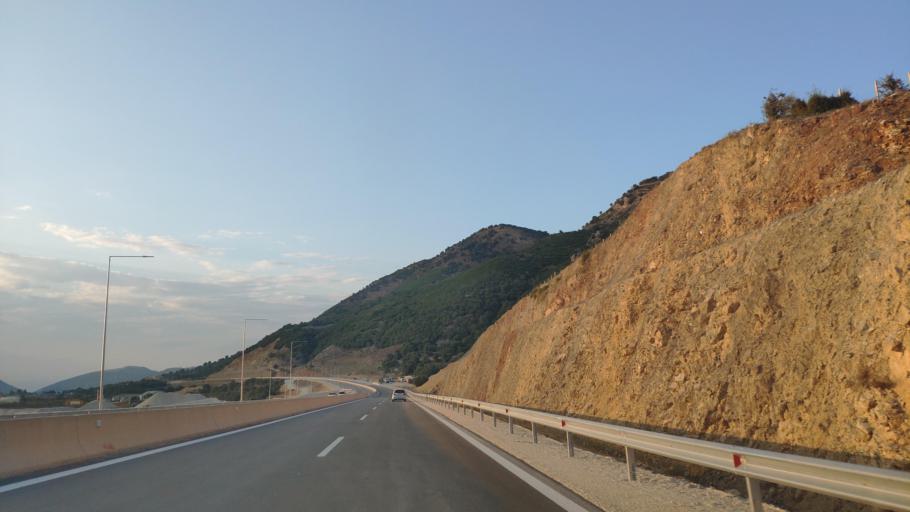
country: GR
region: West Greece
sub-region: Nomos Aitolias kai Akarnanias
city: Katouna
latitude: 38.7857
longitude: 21.1429
